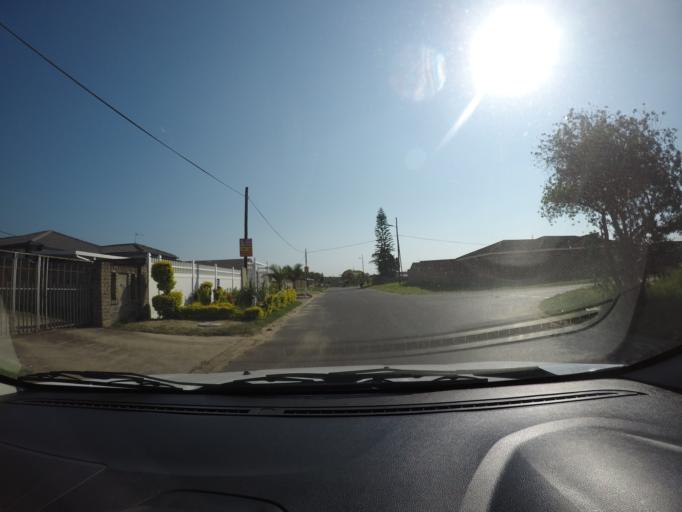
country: ZA
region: KwaZulu-Natal
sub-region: uThungulu District Municipality
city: Richards Bay
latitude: -28.7205
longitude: 32.0384
